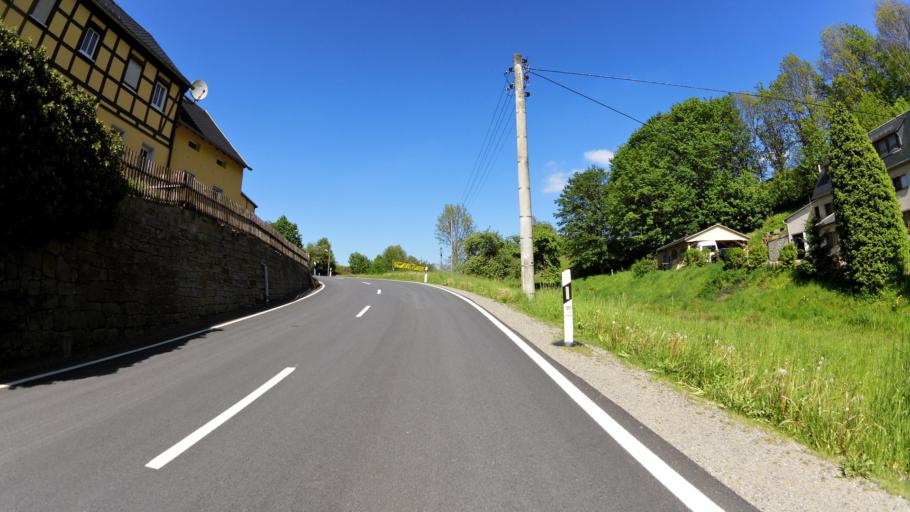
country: DE
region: Saxony
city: Hohnstein
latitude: 50.9804
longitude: 14.1191
